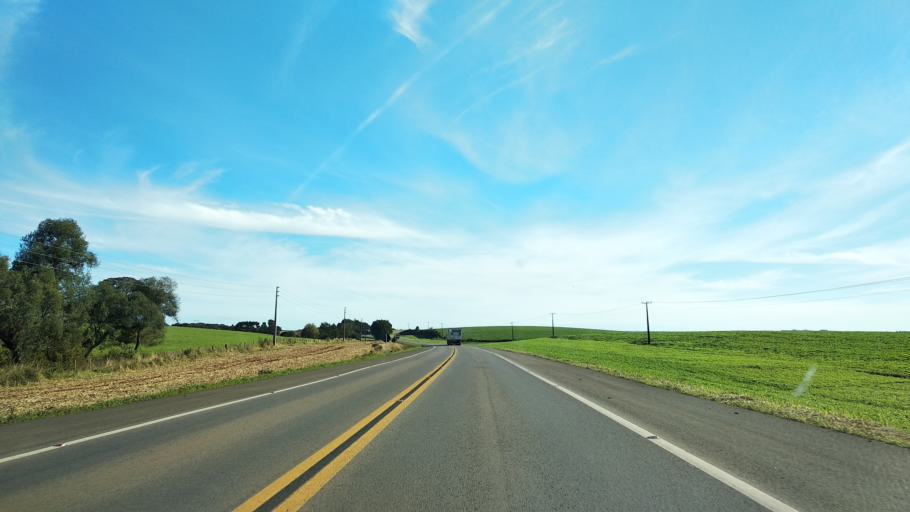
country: BR
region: Santa Catarina
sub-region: Campos Novos
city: Campos Novos
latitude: -27.4915
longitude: -51.3321
